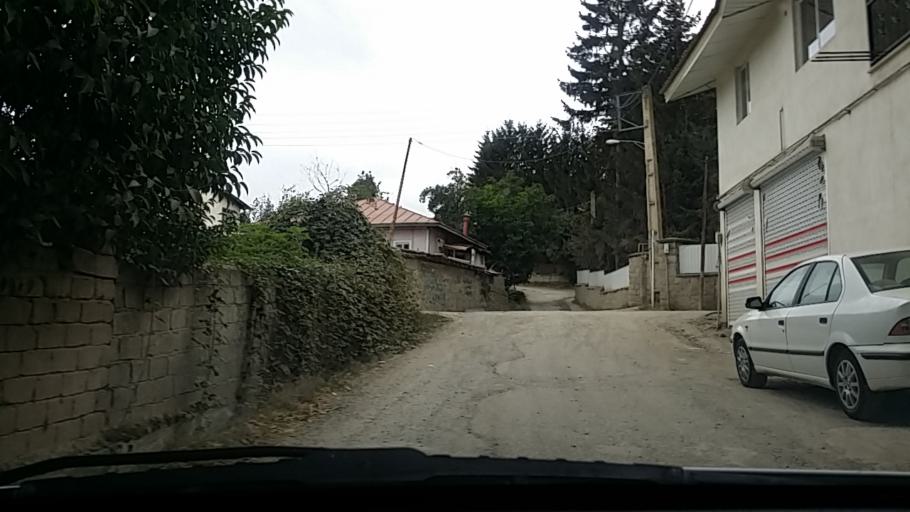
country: IR
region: Mazandaran
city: `Abbasabad
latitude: 36.5104
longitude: 51.1618
